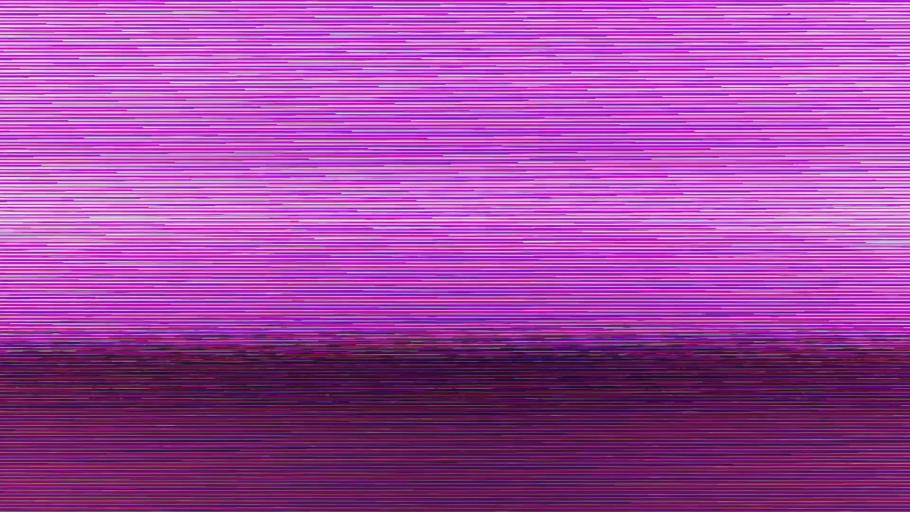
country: US
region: Michigan
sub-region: Berrien County
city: Watervliet
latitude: 42.1785
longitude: -86.2579
